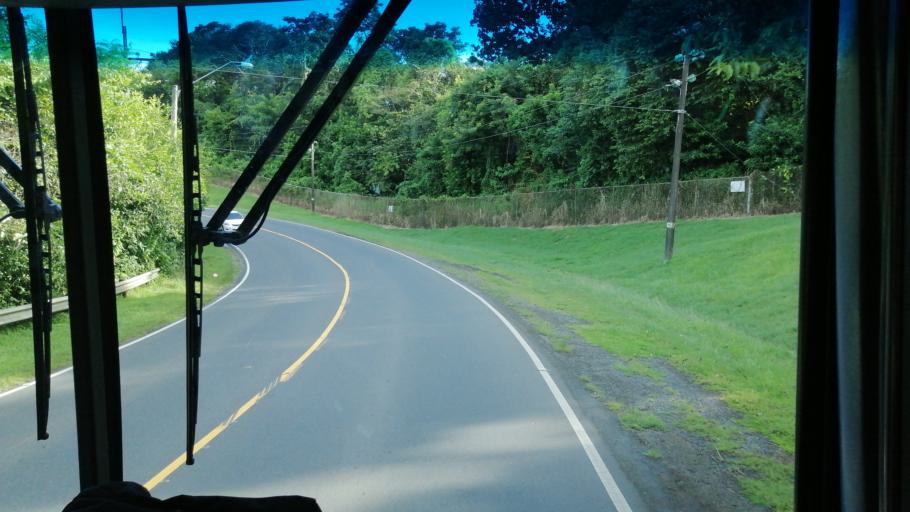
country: PA
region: Panama
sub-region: Distrito de Panama
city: Ancon
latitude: 8.9440
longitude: -79.5918
